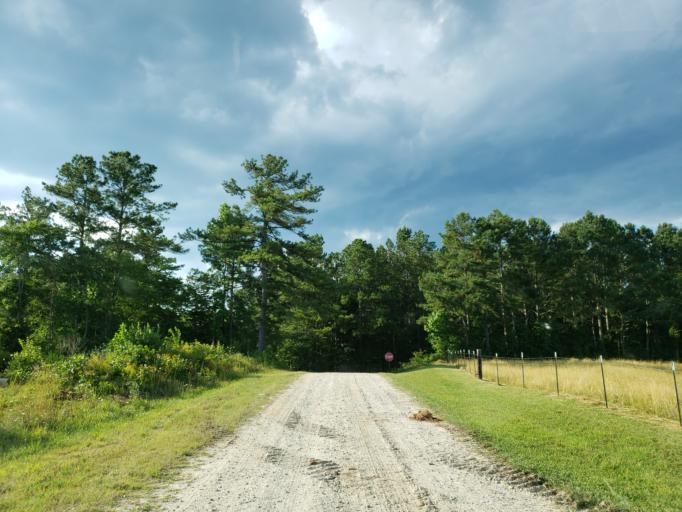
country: US
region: Georgia
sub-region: Haralson County
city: Buchanan
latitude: 33.8561
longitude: -85.2026
